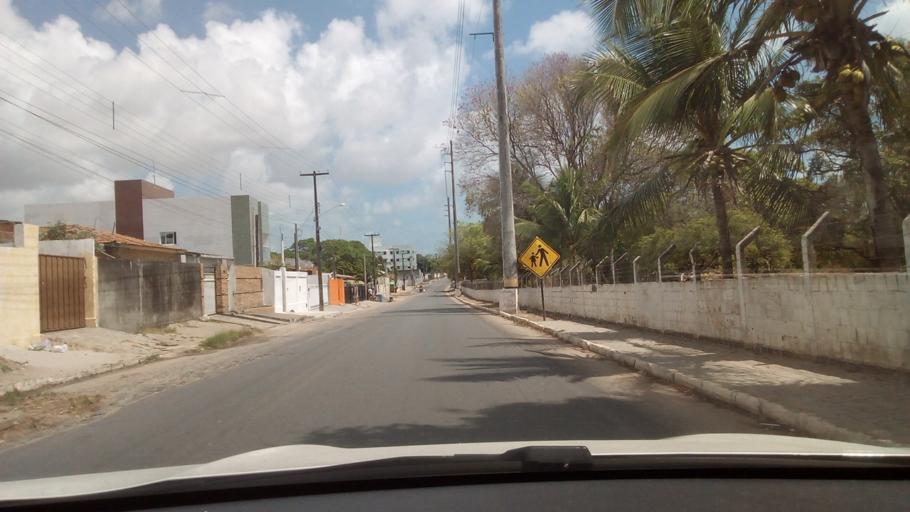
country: BR
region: Paraiba
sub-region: Conde
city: Conde
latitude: -7.2135
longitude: -34.8308
